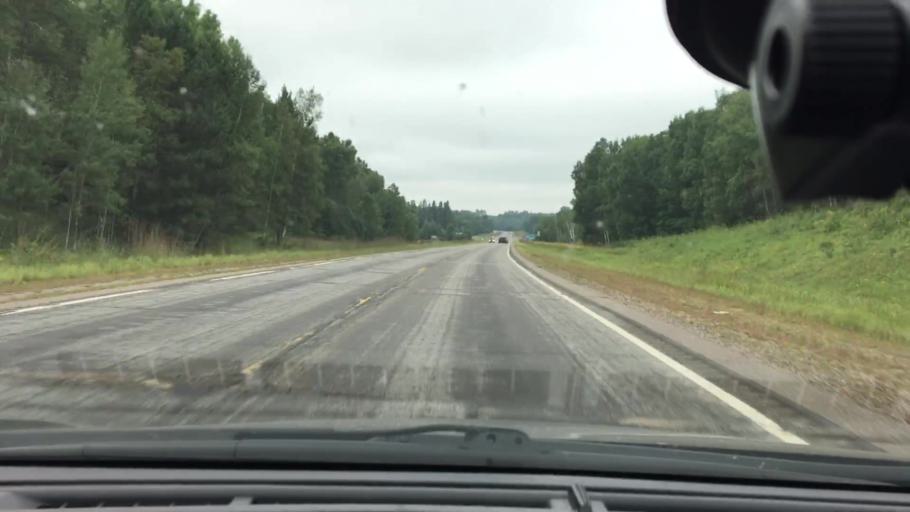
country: US
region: Minnesota
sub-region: Crow Wing County
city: Cross Lake
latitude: 46.6676
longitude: -93.9521
